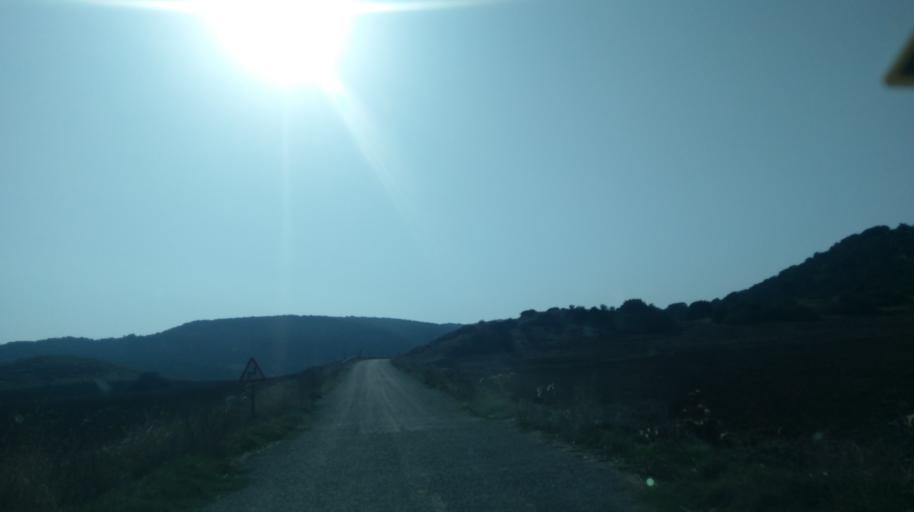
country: CY
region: Ammochostos
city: Rizokarpaso
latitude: 35.5567
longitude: 34.3710
